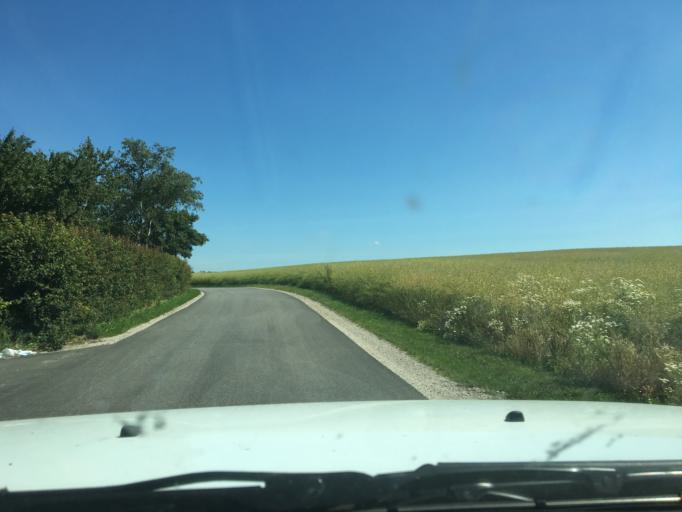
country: DK
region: Central Jutland
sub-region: Horsens Kommune
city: Braedstrup
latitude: 55.9535
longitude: 9.5751
